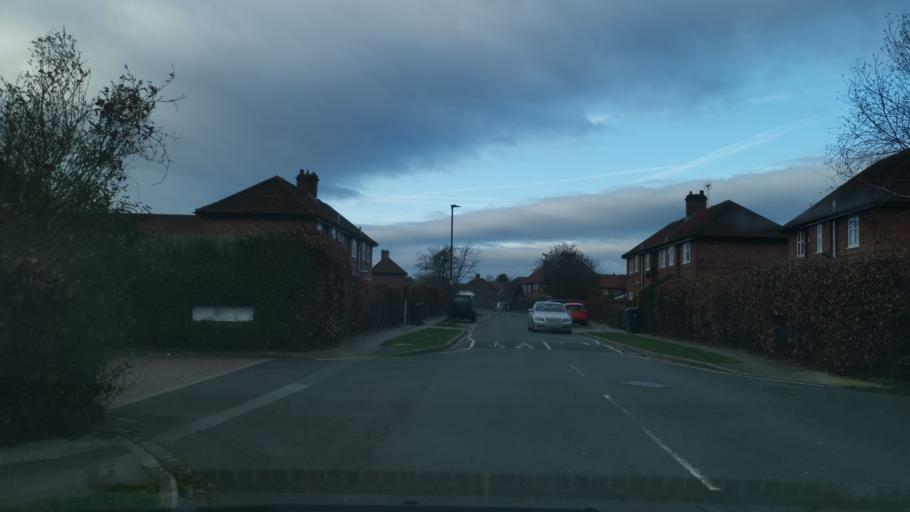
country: GB
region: England
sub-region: City of York
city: Haxby
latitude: 53.9935
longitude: -1.0753
